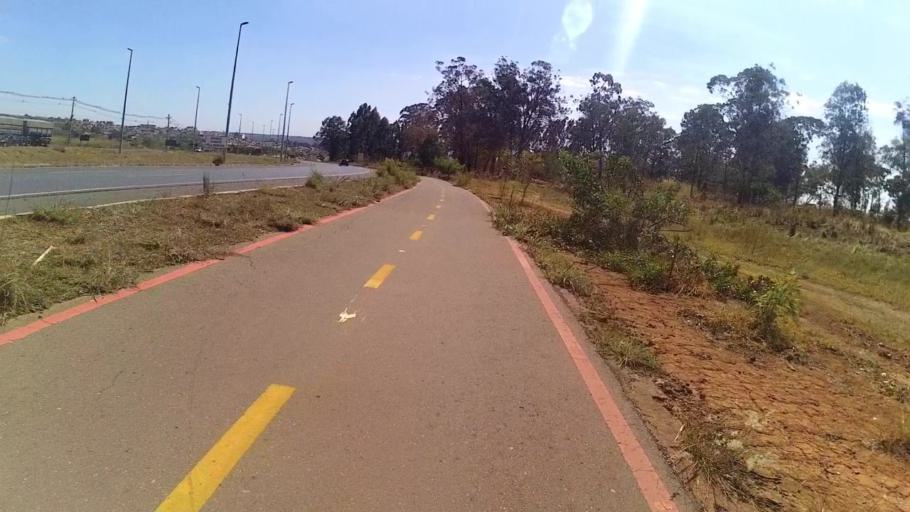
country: BR
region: Federal District
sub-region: Brasilia
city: Brasilia
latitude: -15.6846
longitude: -47.8539
